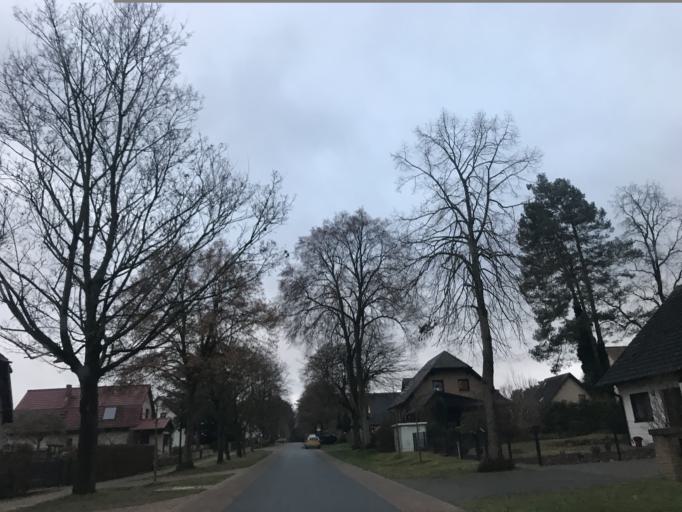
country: DE
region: Brandenburg
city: Rheinsberg
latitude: 53.0909
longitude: 12.8945
